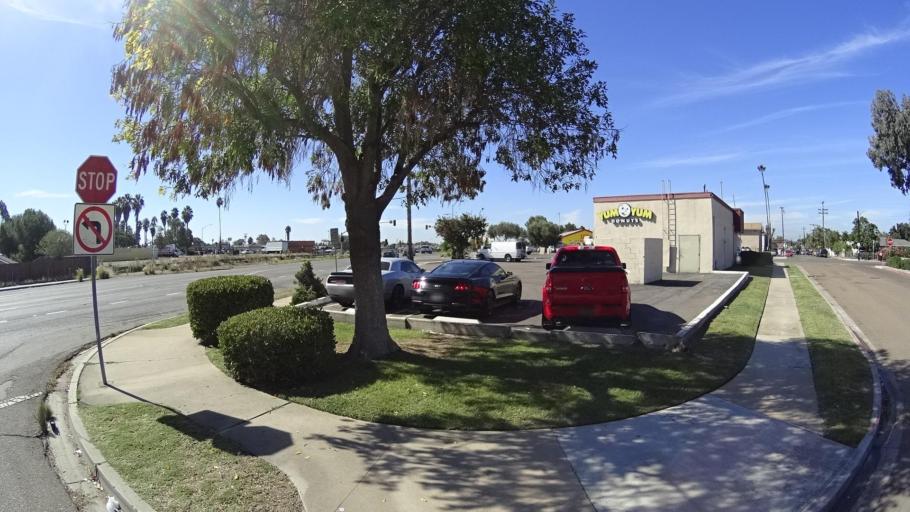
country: US
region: California
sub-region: San Diego County
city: Lemon Grove
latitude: 32.7185
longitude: -117.0251
